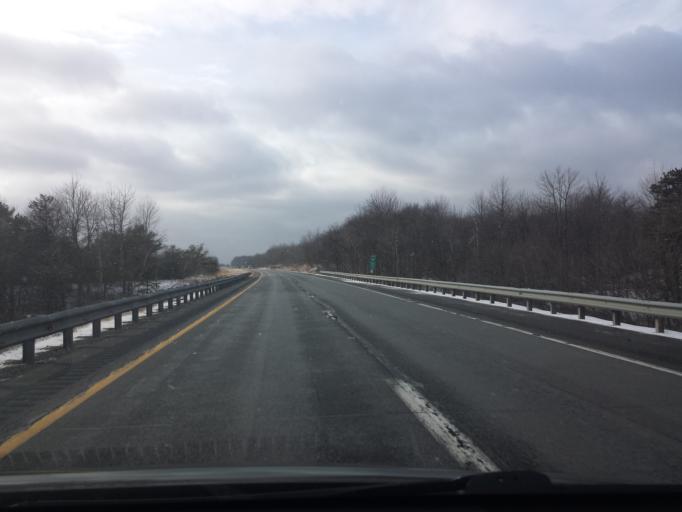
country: US
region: Pennsylvania
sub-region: Monroe County
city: Emerald Lakes
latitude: 41.0728
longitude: -75.4155
